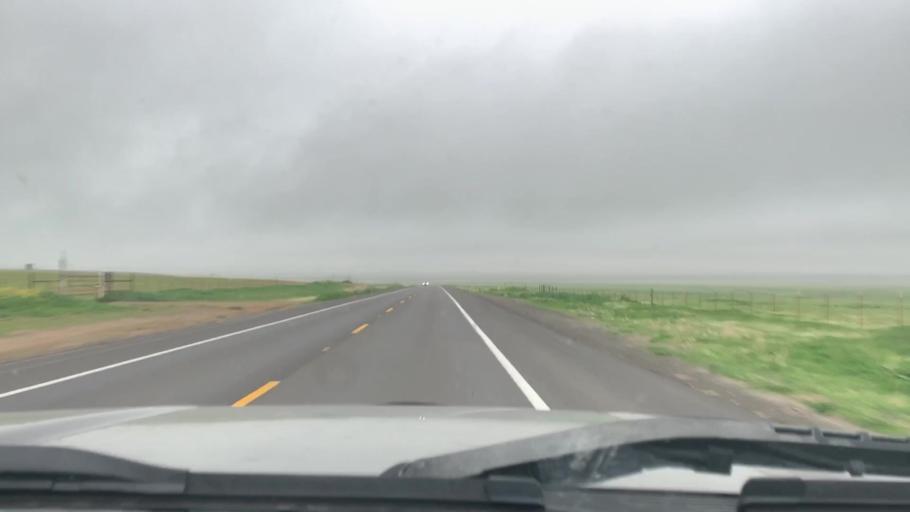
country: US
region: California
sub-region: Kings County
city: Avenal
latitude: 35.7822
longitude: -120.1232
